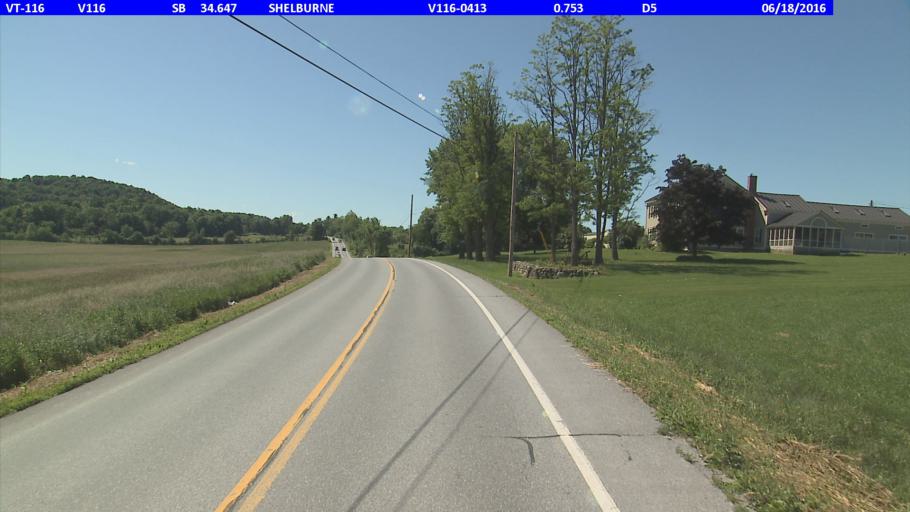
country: US
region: Vermont
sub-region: Chittenden County
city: Hinesburg
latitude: 44.3897
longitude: -73.1423
